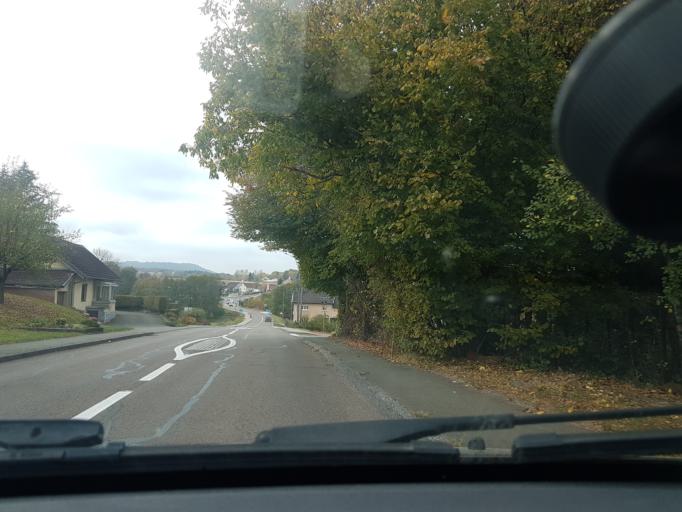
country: FR
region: Franche-Comte
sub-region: Departement de la Haute-Saone
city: Frahier-et-Chatebier
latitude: 47.6621
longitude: 6.7424
